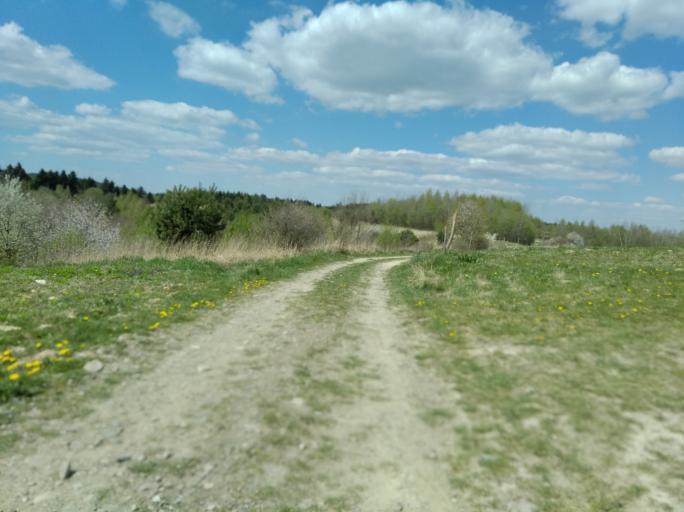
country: PL
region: Subcarpathian Voivodeship
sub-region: Powiat brzozowski
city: Jablonka
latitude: 49.7428
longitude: 22.0853
